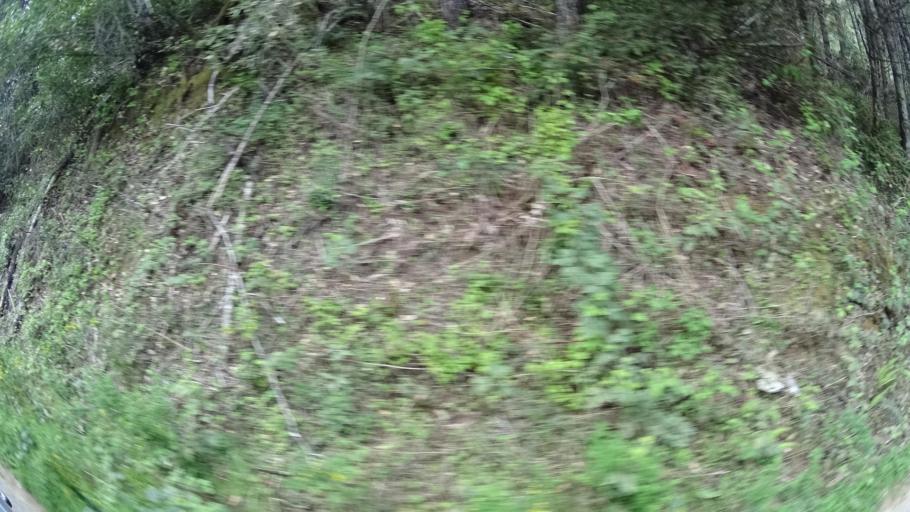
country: US
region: California
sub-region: Humboldt County
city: Redway
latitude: 40.1472
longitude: -123.6294
